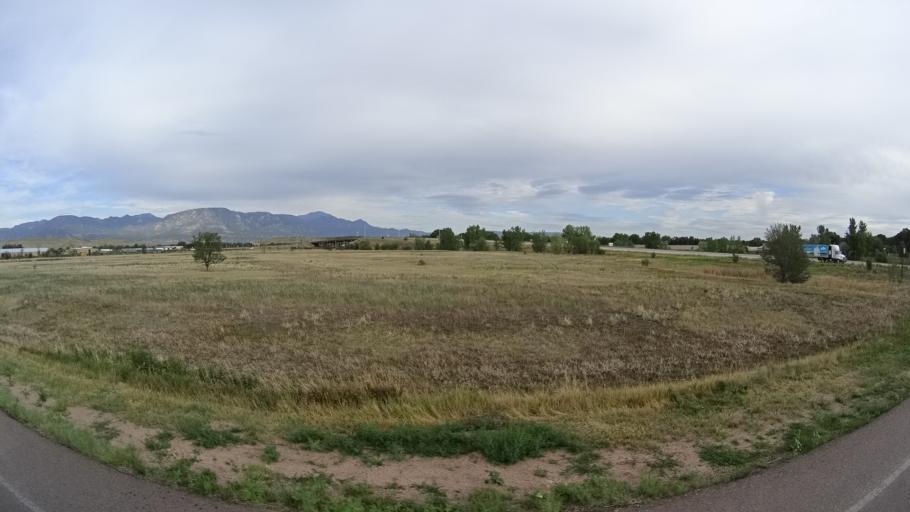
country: US
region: Colorado
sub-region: El Paso County
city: Security-Widefield
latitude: 38.7207
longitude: -104.7125
